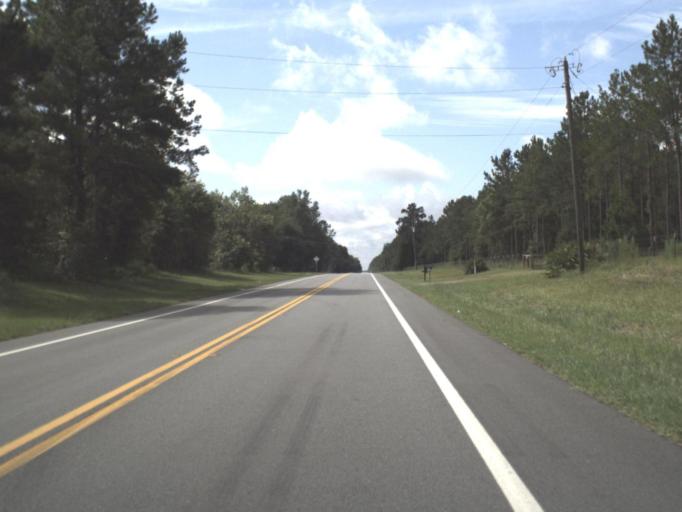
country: US
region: Florida
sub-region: Columbia County
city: Five Points
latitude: 30.4145
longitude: -82.6366
